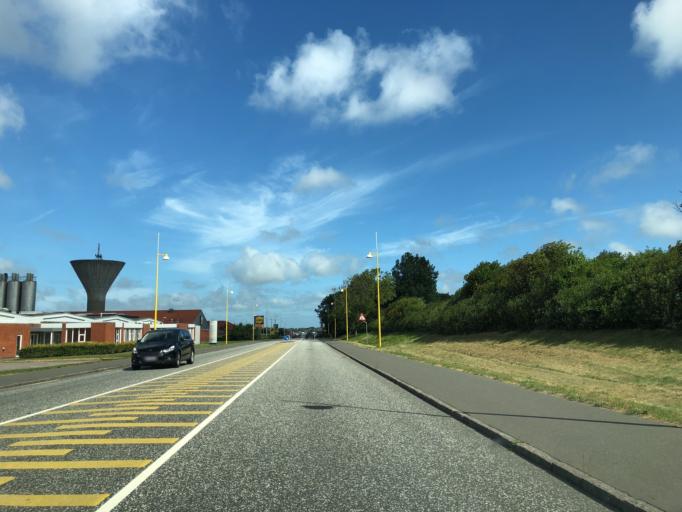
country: DK
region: Central Jutland
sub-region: Struer Kommune
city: Struer
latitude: 56.4850
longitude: 8.5836
